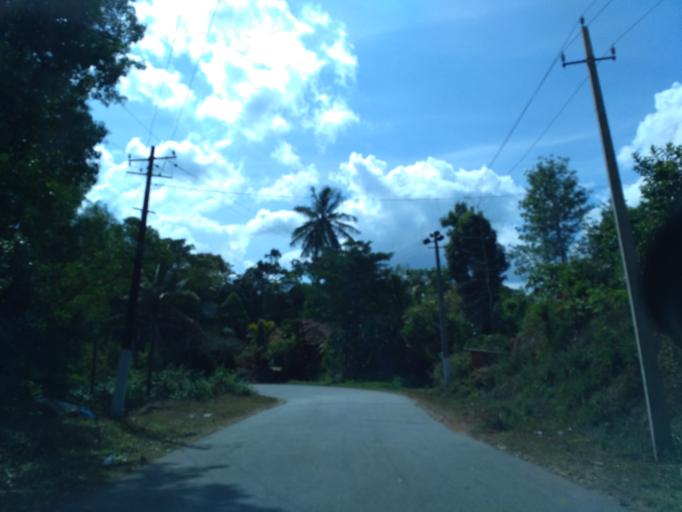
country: IN
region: Karnataka
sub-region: Kodagu
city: Madikeri
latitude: 12.3731
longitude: 75.6073
